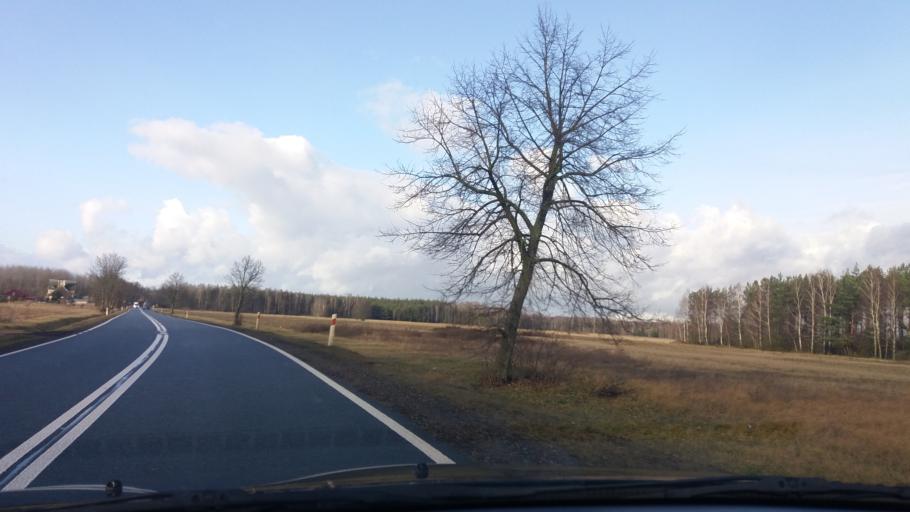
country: PL
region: Masovian Voivodeship
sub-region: Powiat przasnyski
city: Chorzele
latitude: 53.2742
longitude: 20.9002
